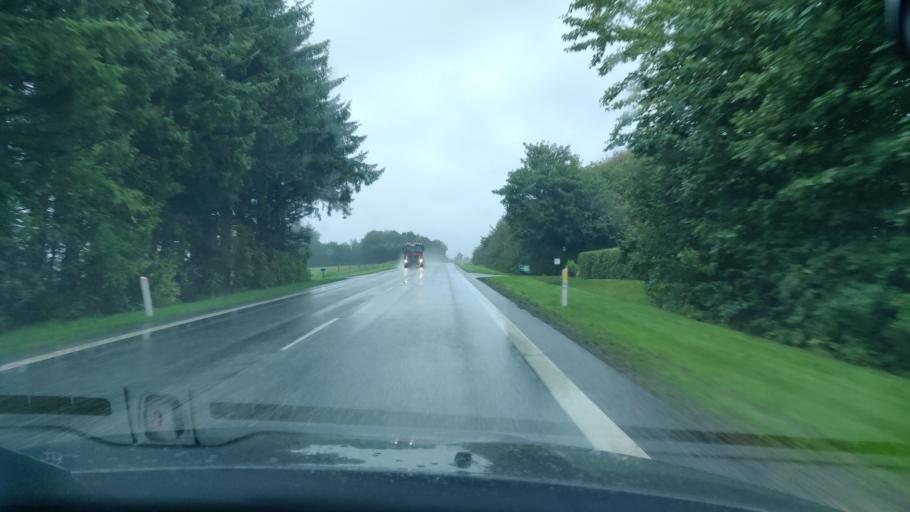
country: DK
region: North Denmark
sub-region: Thisted Kommune
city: Hurup
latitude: 56.8365
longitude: 8.5116
